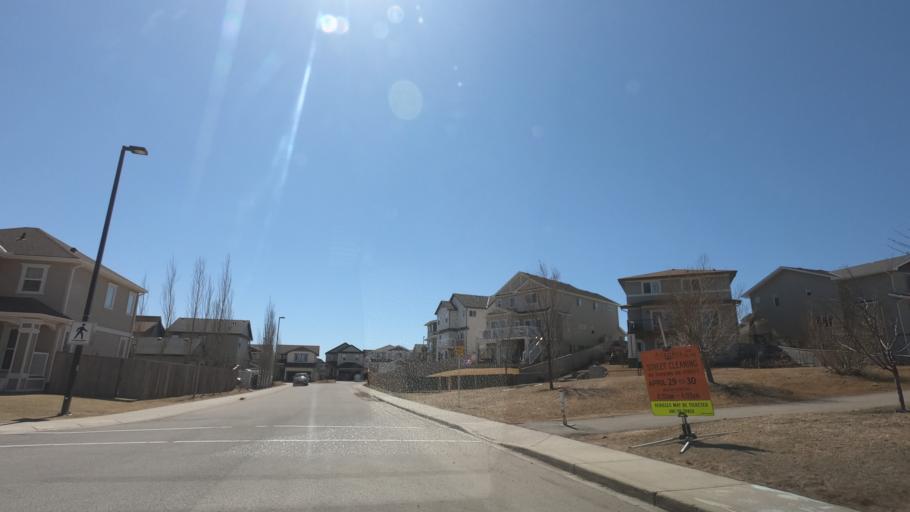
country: CA
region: Alberta
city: Airdrie
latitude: 51.3031
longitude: -114.0469
